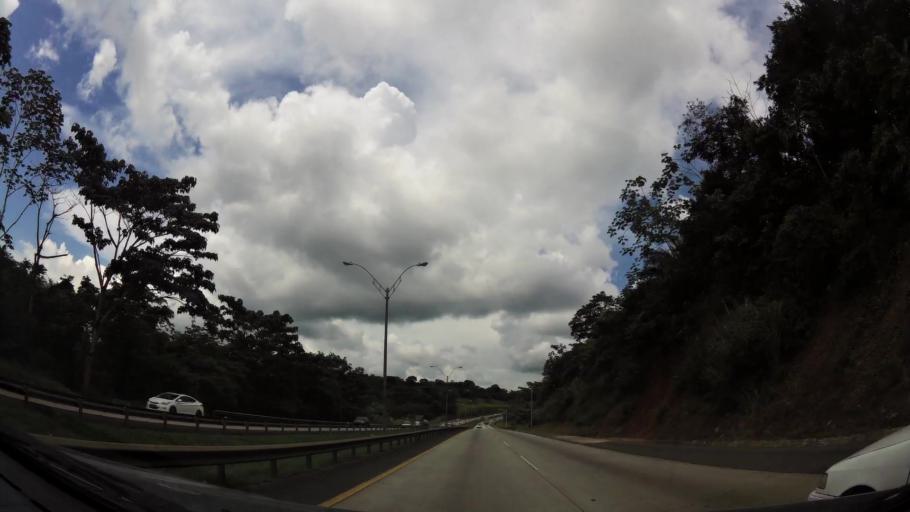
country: PA
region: Panama
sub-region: Distrito Arraijan
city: Arraijan
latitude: 8.9794
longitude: -79.6465
